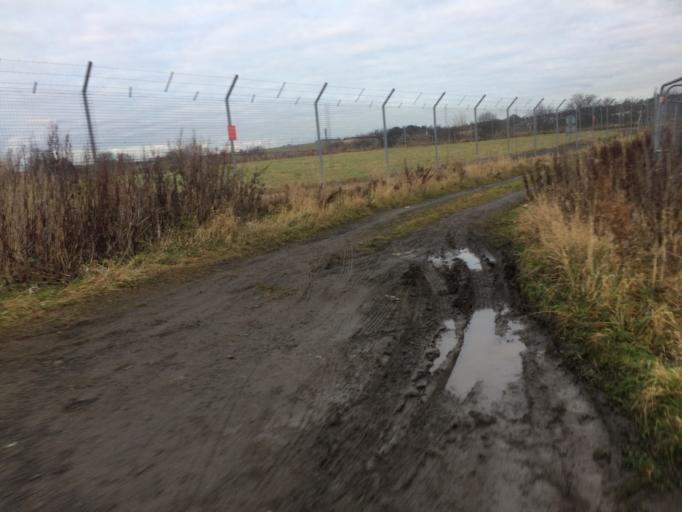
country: GB
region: Scotland
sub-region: Edinburgh
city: Currie
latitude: 55.9414
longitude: -3.3251
